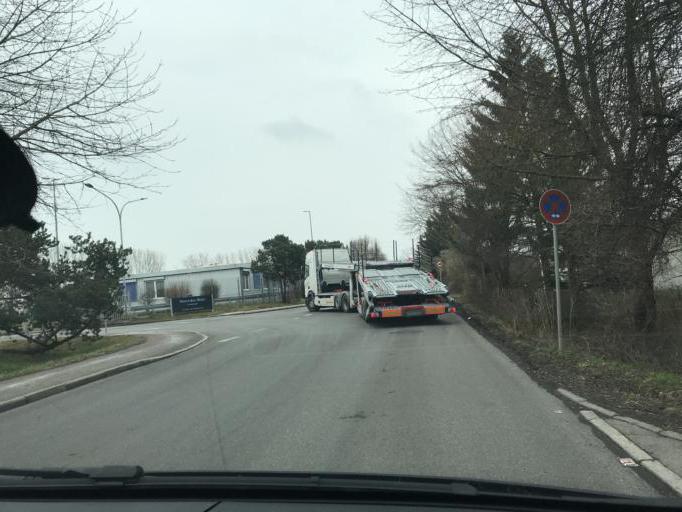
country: DE
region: Baden-Wuerttemberg
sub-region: Regierungsbezirk Stuttgart
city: Boeblingen
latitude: 48.6921
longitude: 8.9845
